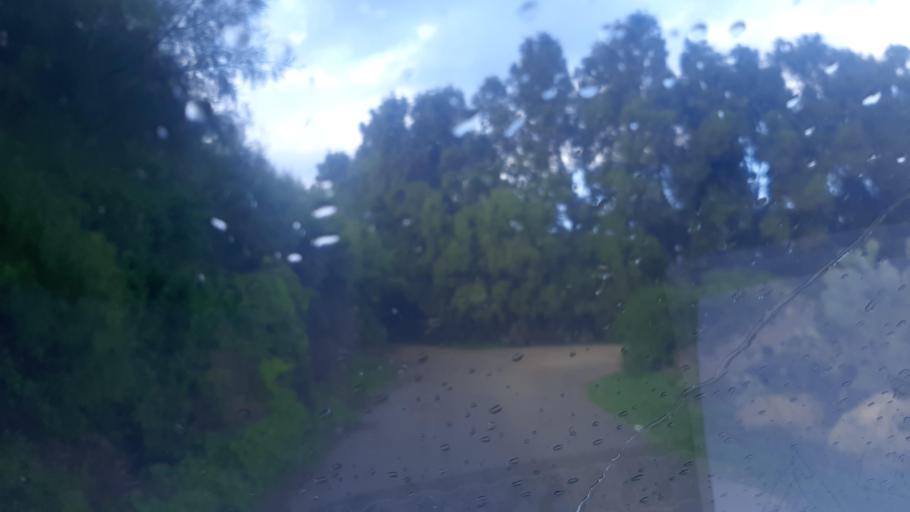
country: TN
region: Nabul
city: Manzil Bu Zalafah
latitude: 36.7371
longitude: 10.5295
